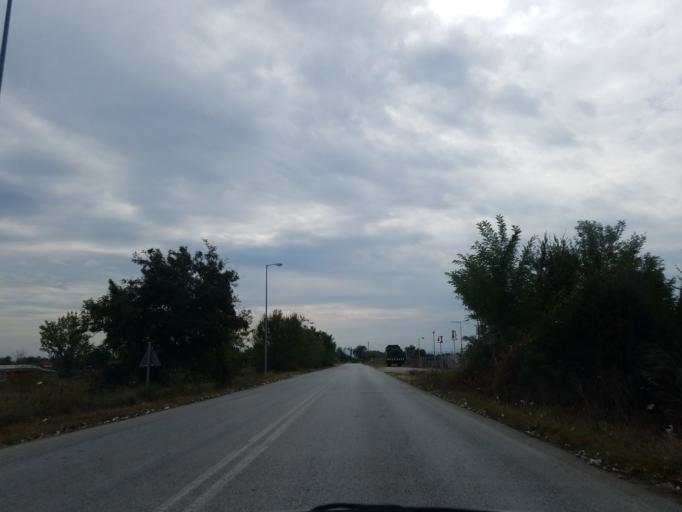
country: GR
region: Thessaly
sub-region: Nomos Kardhitsas
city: Sofades
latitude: 39.3320
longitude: 22.0870
